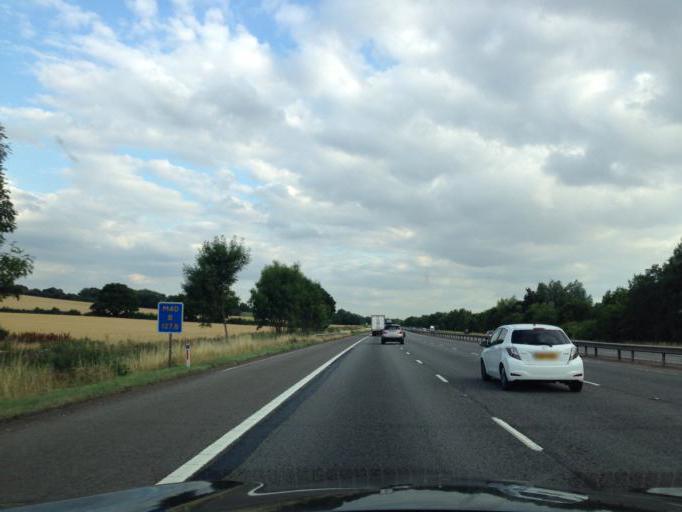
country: GB
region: England
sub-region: Oxfordshire
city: Hanwell
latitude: 52.1056
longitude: -1.3586
